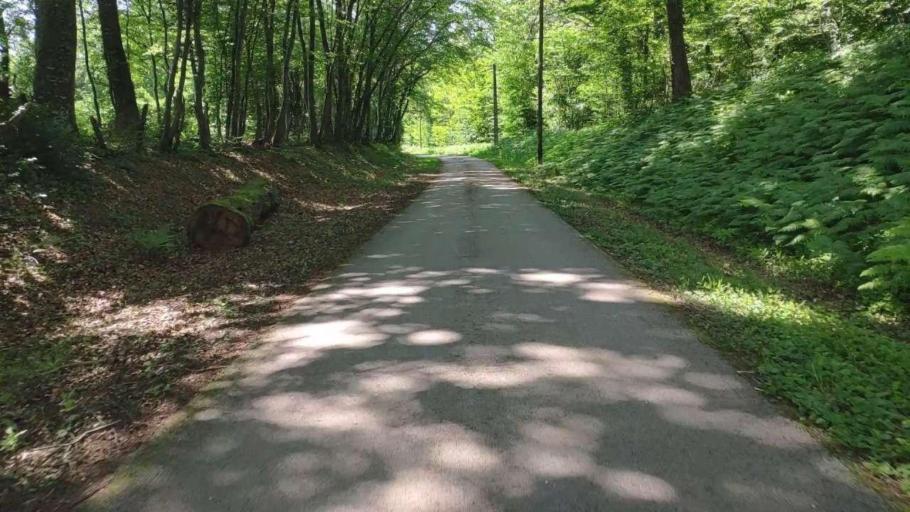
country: FR
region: Franche-Comte
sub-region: Departement du Jura
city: Bletterans
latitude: 46.8042
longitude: 5.4164
